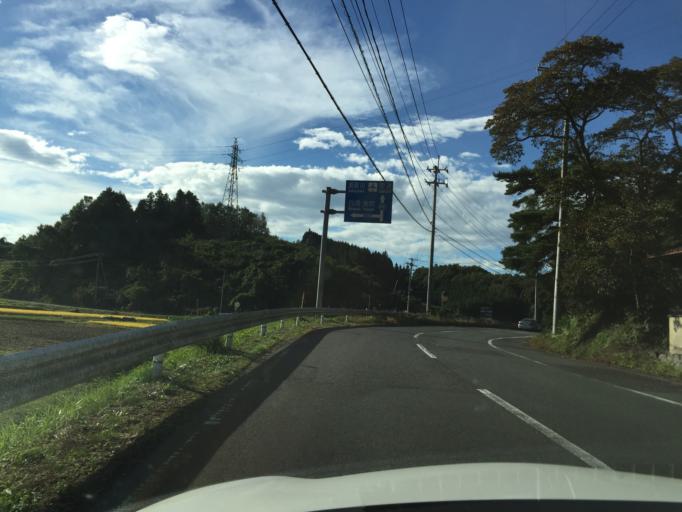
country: JP
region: Fukushima
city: Ishikawa
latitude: 37.1840
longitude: 140.4602
